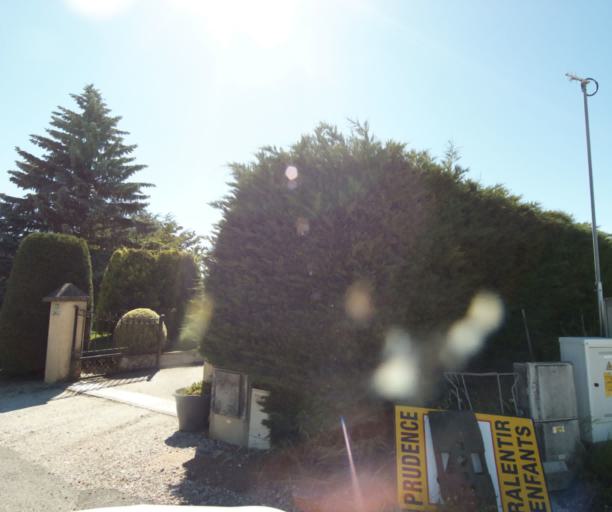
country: FR
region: Rhone-Alpes
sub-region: Departement de la Haute-Savoie
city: Saint-Cergues
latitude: 46.2595
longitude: 6.3275
